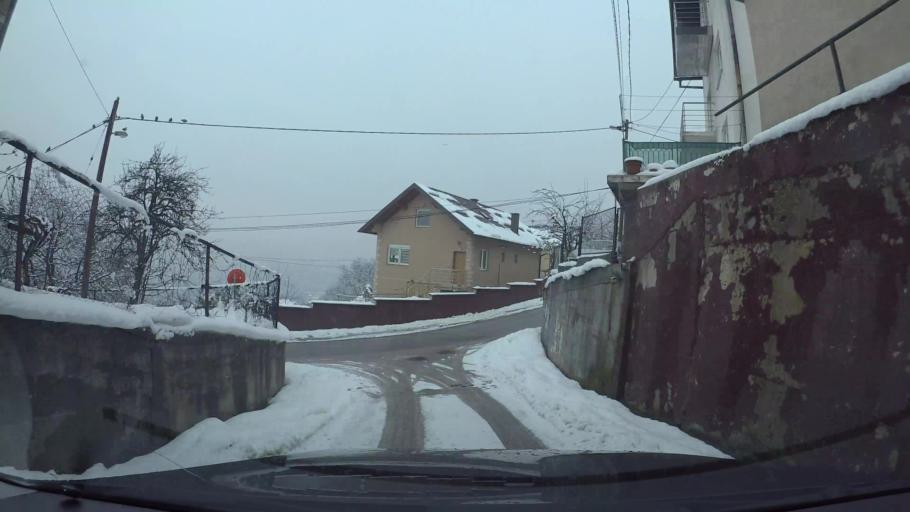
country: BA
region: Federation of Bosnia and Herzegovina
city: Kobilja Glava
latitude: 43.8484
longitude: 18.4108
